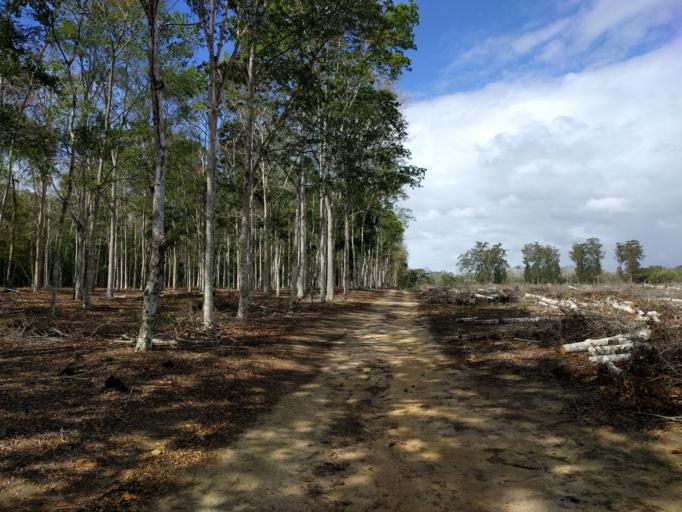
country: BR
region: Espirito Santo
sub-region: Linhares
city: Linhares
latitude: -19.1460
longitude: -40.0714
